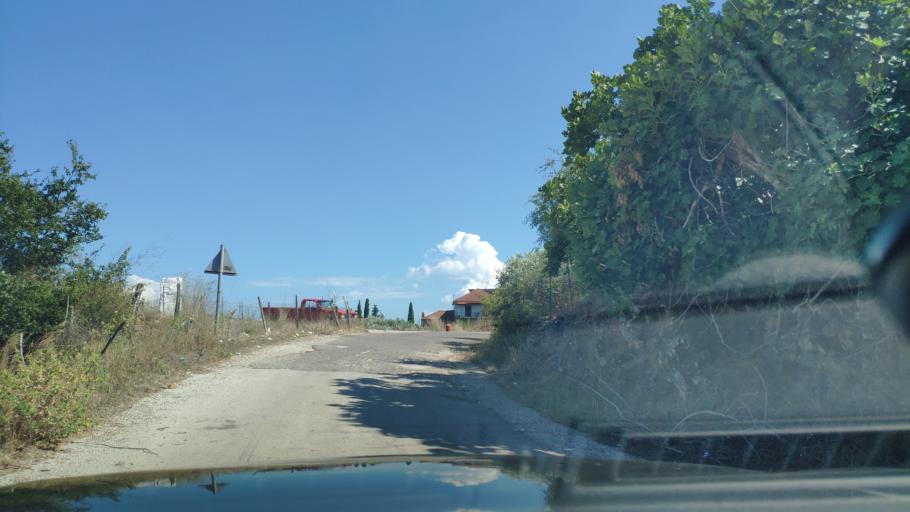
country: GR
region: West Greece
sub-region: Nomos Aitolias kai Akarnanias
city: Katouna
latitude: 38.7919
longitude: 21.1149
